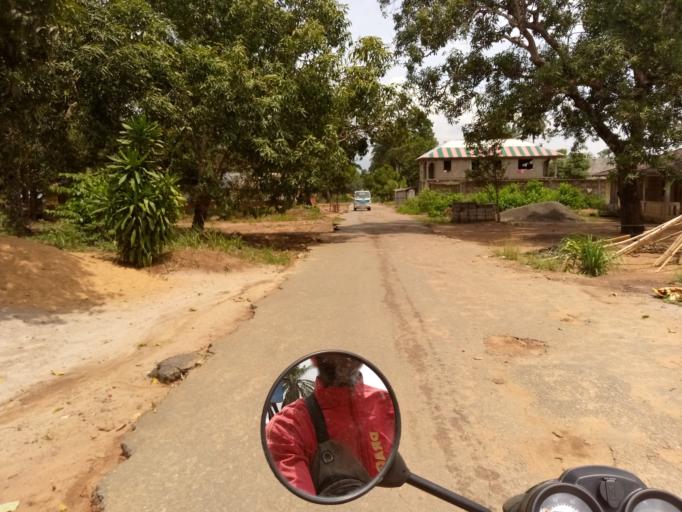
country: SL
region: Western Area
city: Waterloo
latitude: 8.3345
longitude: -13.0102
